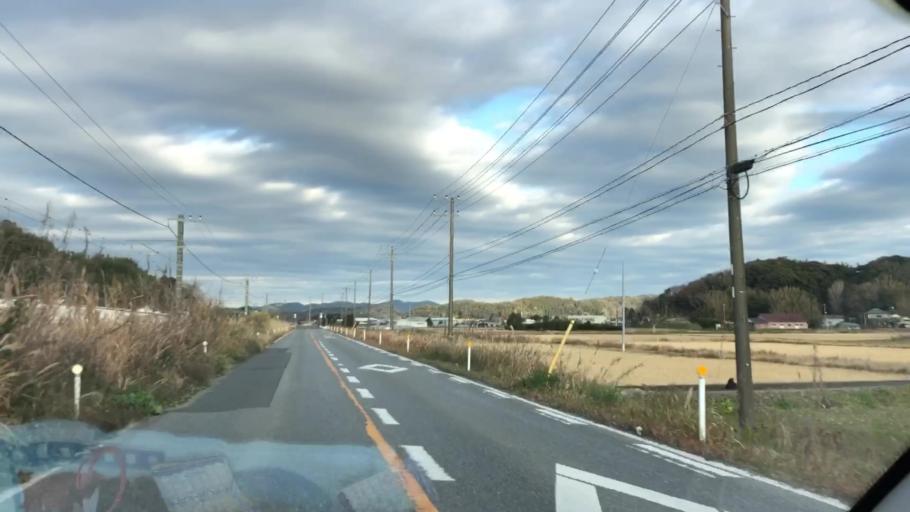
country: JP
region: Chiba
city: Tateyama
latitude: 34.9937
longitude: 139.9201
